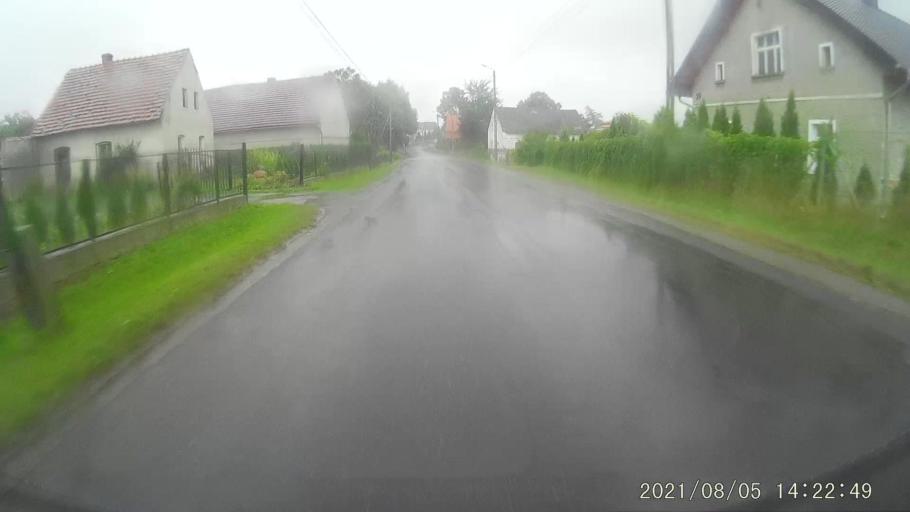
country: PL
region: Opole Voivodeship
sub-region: Powiat nyski
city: Korfantow
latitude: 50.4789
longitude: 17.6530
